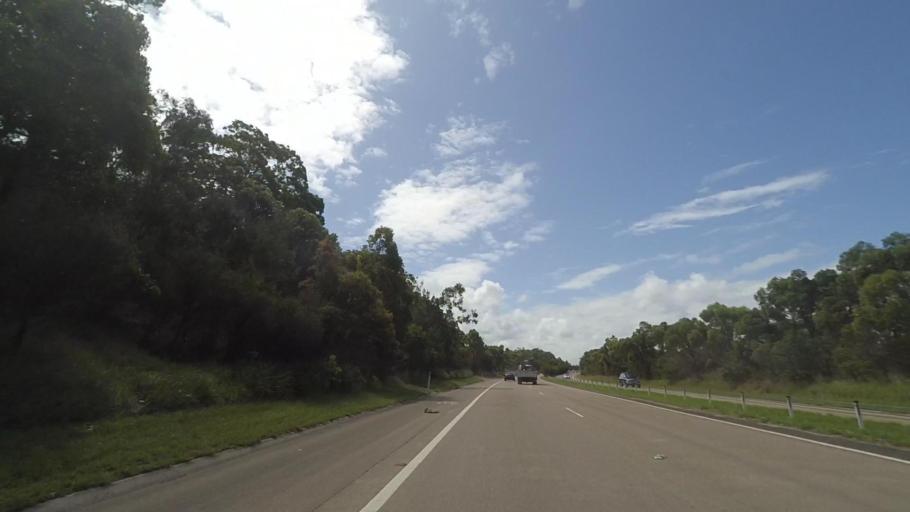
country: AU
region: New South Wales
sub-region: Lake Macquarie Shire
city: Gateshead
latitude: -32.9813
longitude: 151.6808
